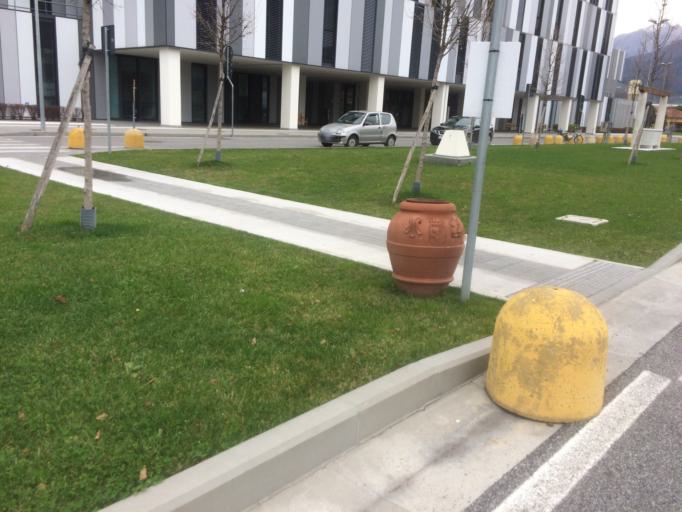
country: IT
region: Tuscany
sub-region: Provincia di Massa-Carrara
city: Massa
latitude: 44.0189
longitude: 10.1004
